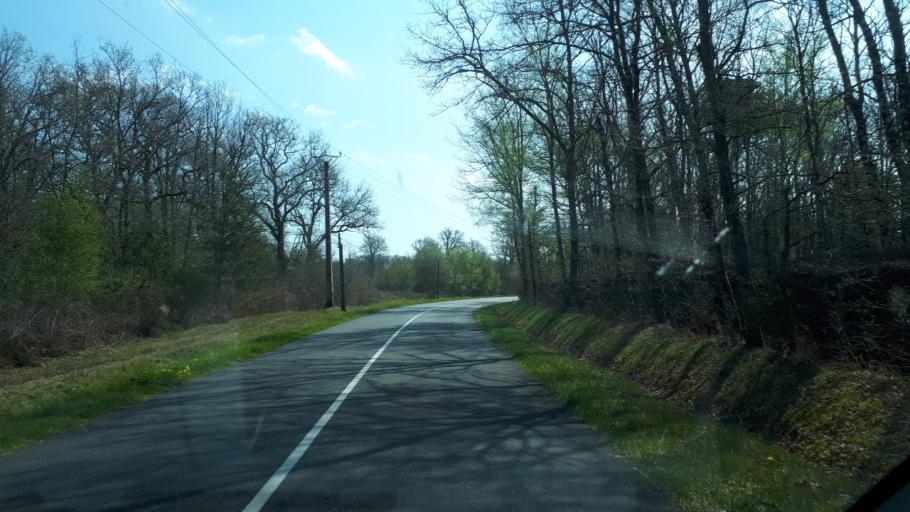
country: FR
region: Centre
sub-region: Departement du Loir-et-Cher
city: Selles-Saint-Denis
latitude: 47.3424
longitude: 1.8998
